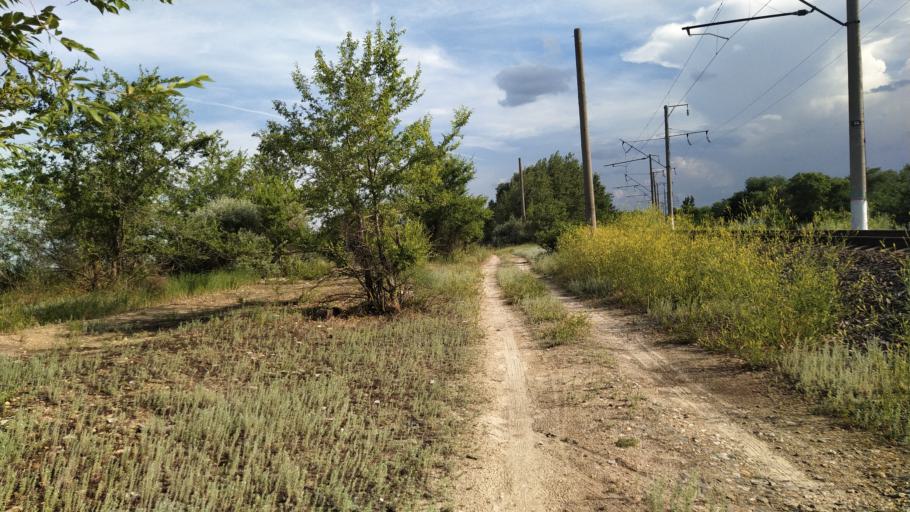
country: RU
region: Rostov
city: Bataysk
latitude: 47.1203
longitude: 39.7130
